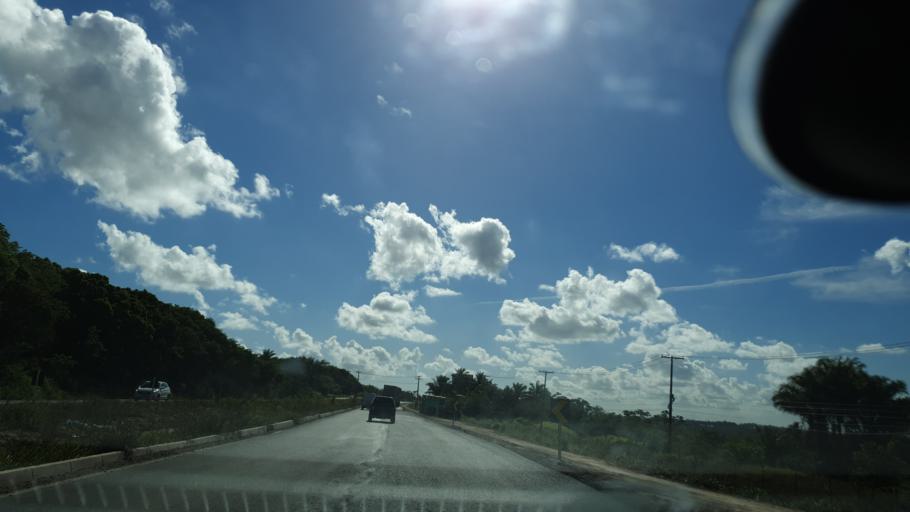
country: BR
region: Bahia
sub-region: Camacari
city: Camacari
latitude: -12.6806
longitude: -38.2858
